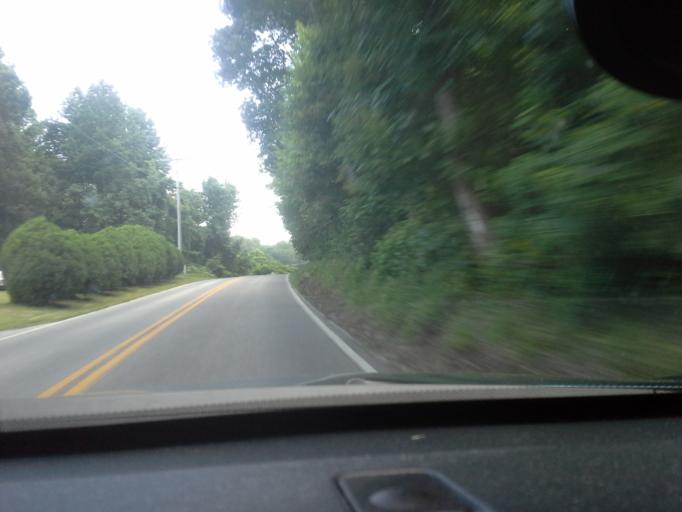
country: US
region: Maryland
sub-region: Calvert County
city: Prince Frederick
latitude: 38.5902
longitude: -76.5434
